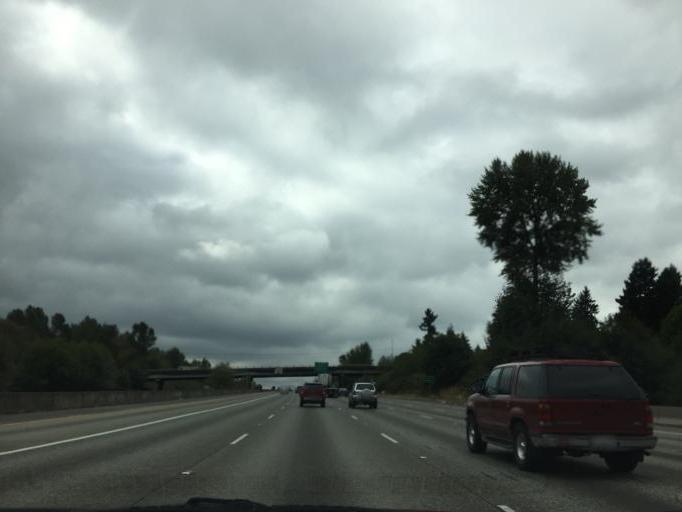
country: US
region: Washington
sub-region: King County
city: SeaTac
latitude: 47.4457
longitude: -122.2677
